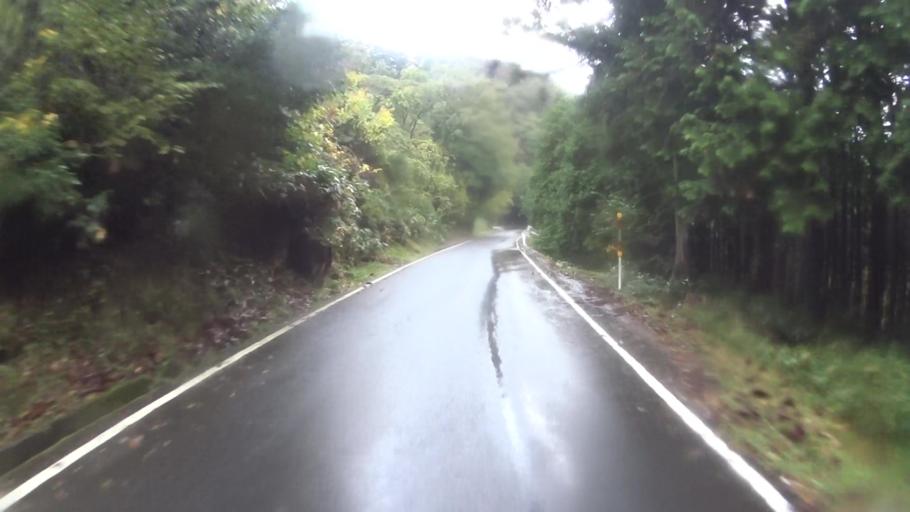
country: JP
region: Kyoto
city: Miyazu
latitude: 35.4827
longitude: 135.1535
